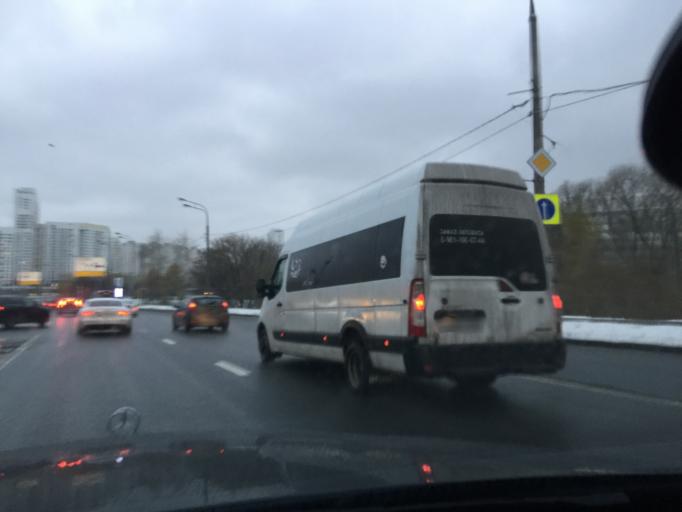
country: RU
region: Moscow
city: Troparevo
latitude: 55.6531
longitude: 37.4795
